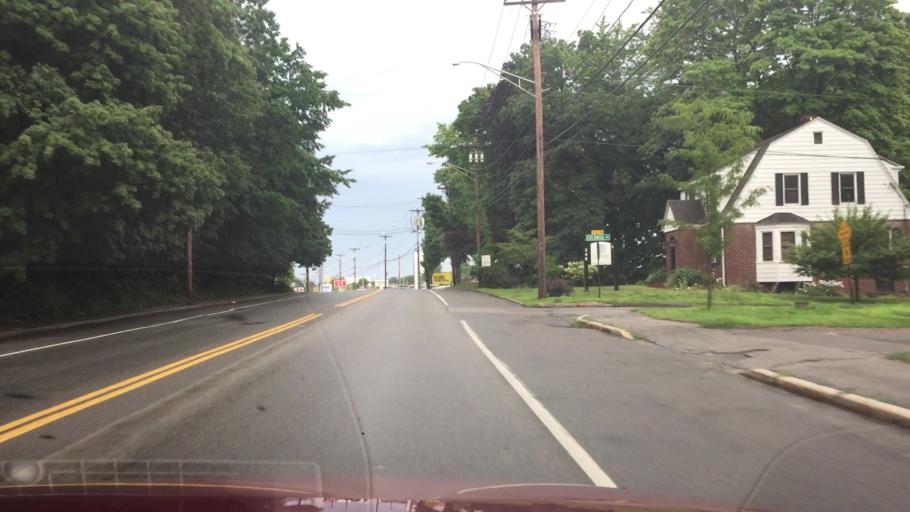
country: US
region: Maine
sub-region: Cumberland County
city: Westbrook
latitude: 43.6790
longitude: -70.3405
